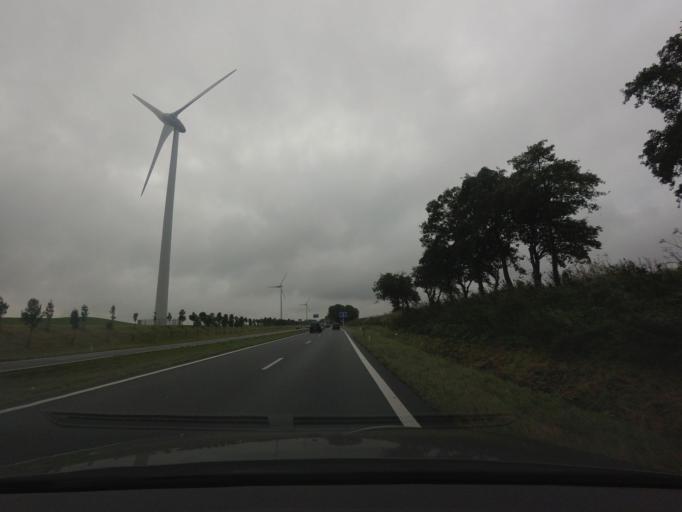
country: NL
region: North Holland
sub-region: Gemeente Langedijk
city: Broek op Langedijk
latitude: 52.6523
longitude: 4.7979
